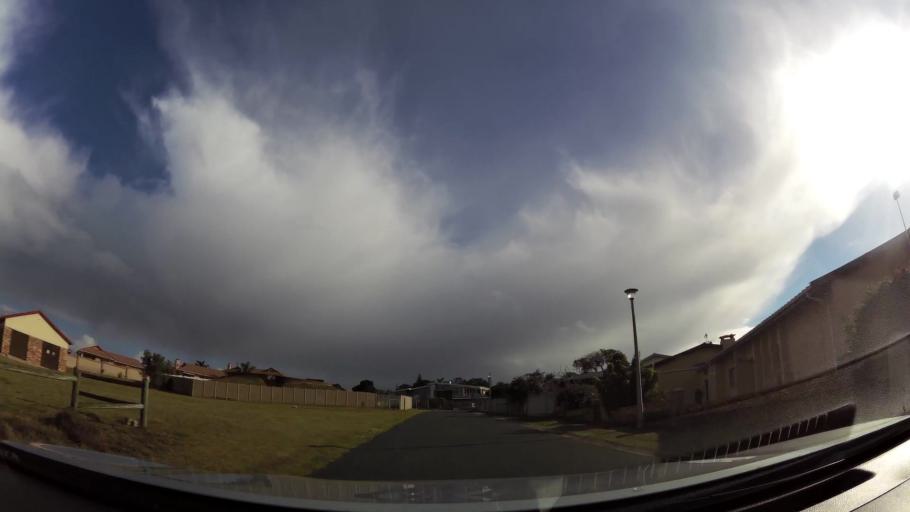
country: ZA
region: Western Cape
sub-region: Eden District Municipality
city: Mossel Bay
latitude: -34.1855
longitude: 22.1318
